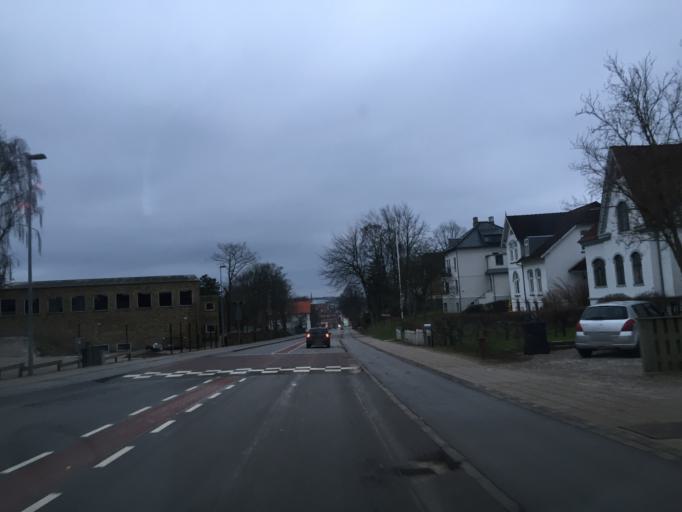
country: DK
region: South Denmark
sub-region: Haderslev Kommune
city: Haderslev
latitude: 55.2581
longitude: 9.4926
